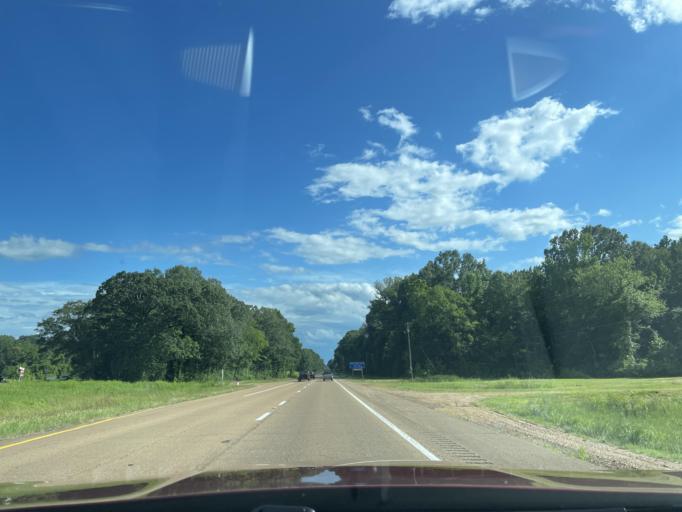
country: US
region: Mississippi
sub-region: Madison County
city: Flora
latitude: 32.4736
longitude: -90.2885
